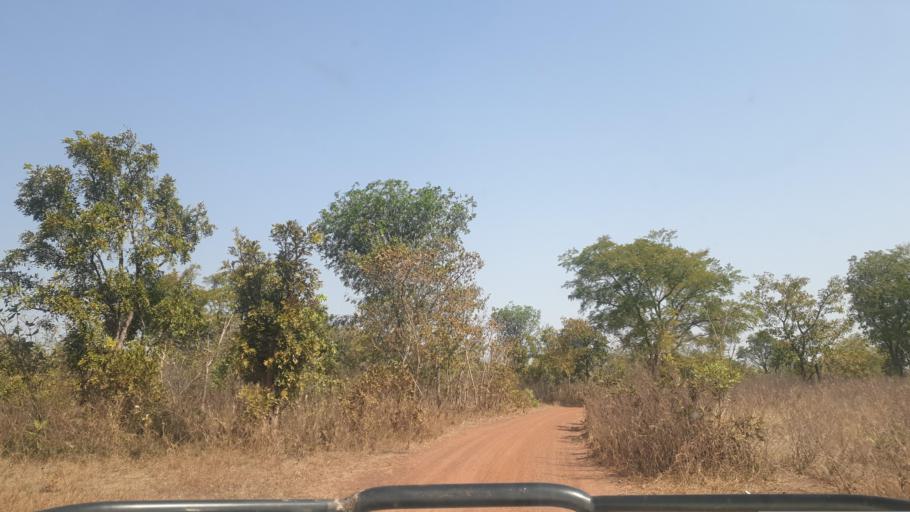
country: ML
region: Sikasso
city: Kolondieba
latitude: 10.8700
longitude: -6.7789
